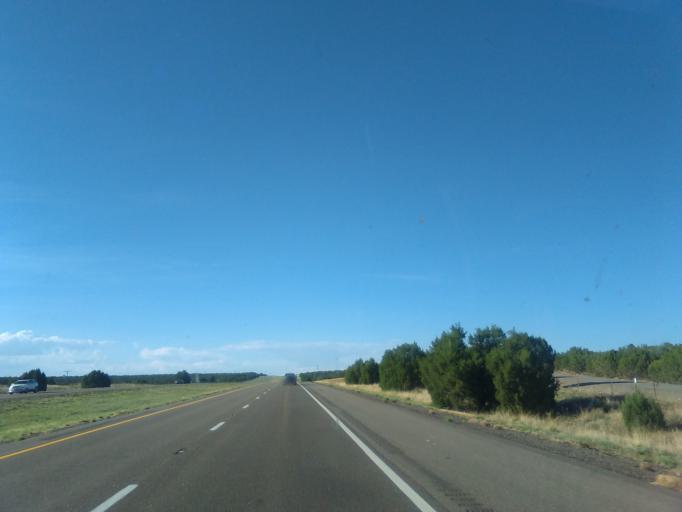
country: US
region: New Mexico
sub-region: San Miguel County
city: Las Vegas
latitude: 35.4666
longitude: -105.2762
